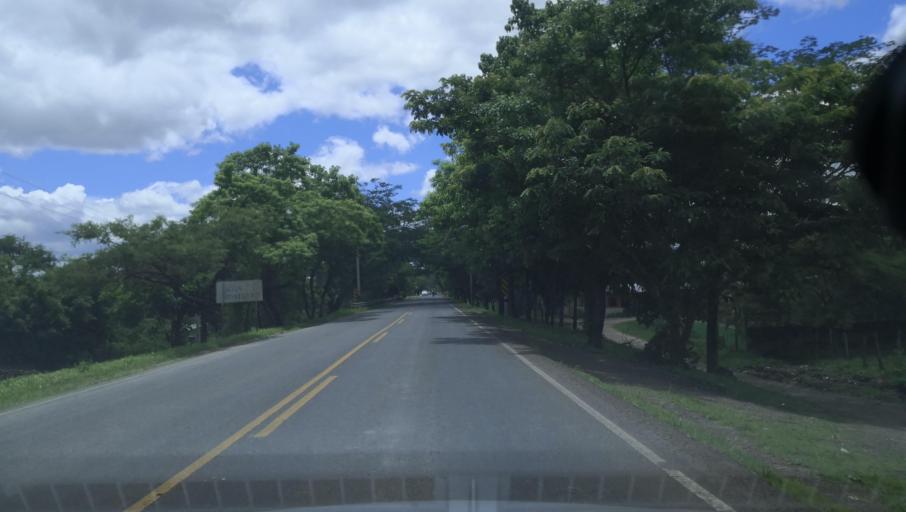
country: NI
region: Esteli
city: Esteli
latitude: 13.1600
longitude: -86.3694
